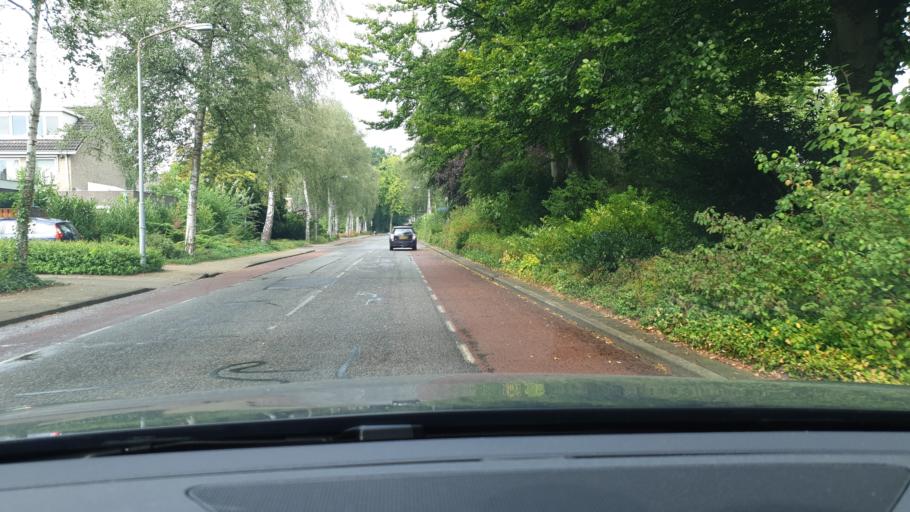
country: NL
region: North Brabant
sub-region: Gemeente Veldhoven
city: Oerle
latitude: 51.4158
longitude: 5.3848
